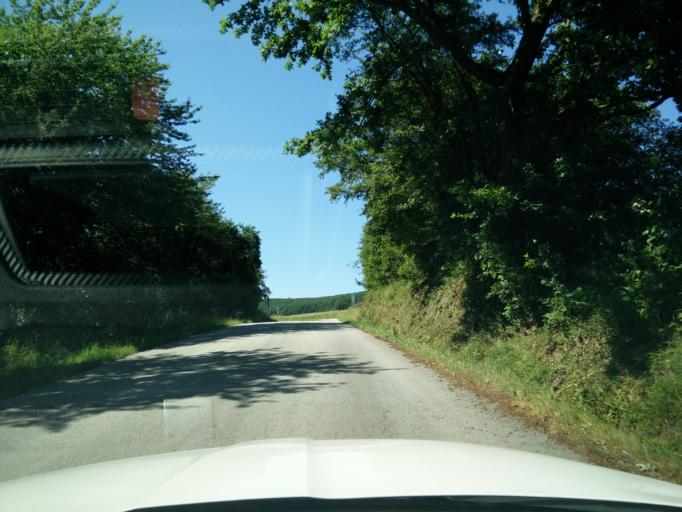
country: SK
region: Nitriansky
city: Prievidza
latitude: 48.7811
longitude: 18.6969
